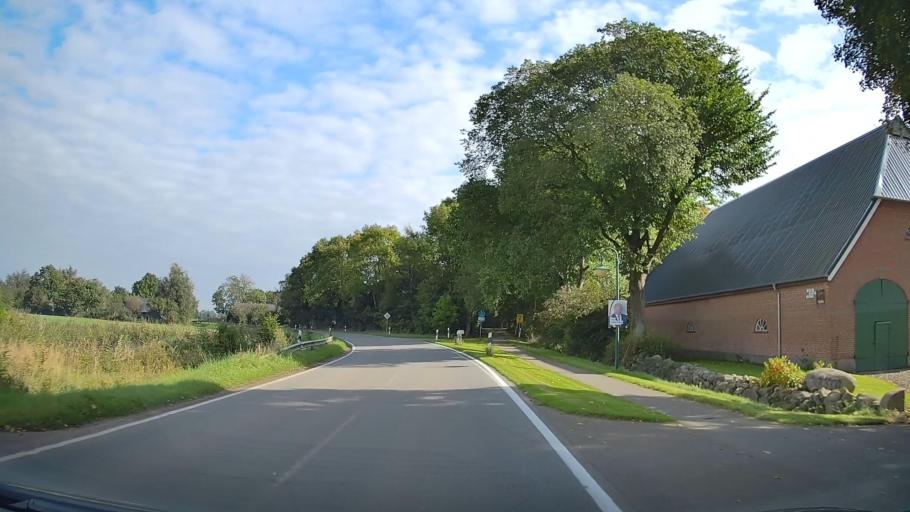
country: DE
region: Schleswig-Holstein
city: Gremersdorf
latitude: 54.3432
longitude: 10.8990
